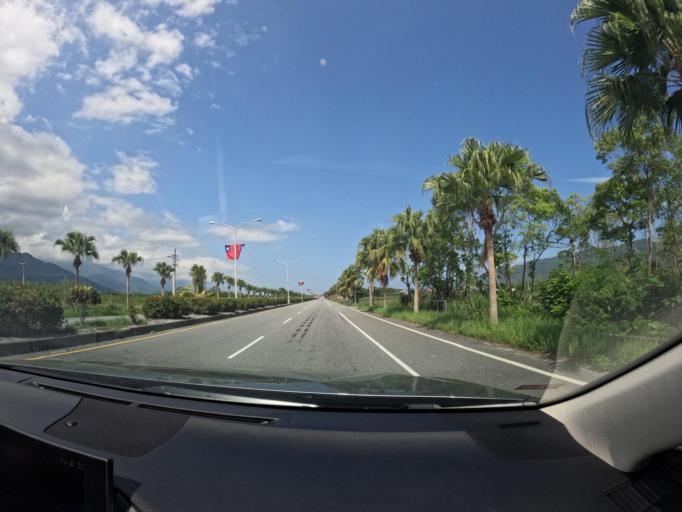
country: TW
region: Taiwan
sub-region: Hualien
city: Hualian
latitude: 23.8743
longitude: 121.5382
